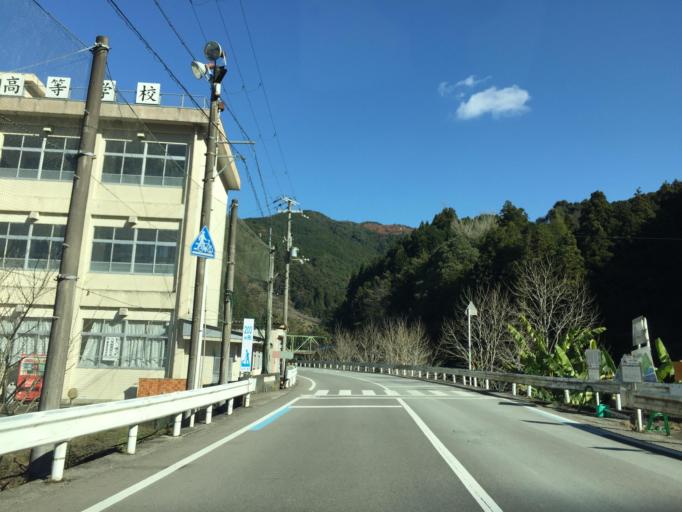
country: JP
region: Wakayama
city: Iwade
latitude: 34.1395
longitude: 135.4160
